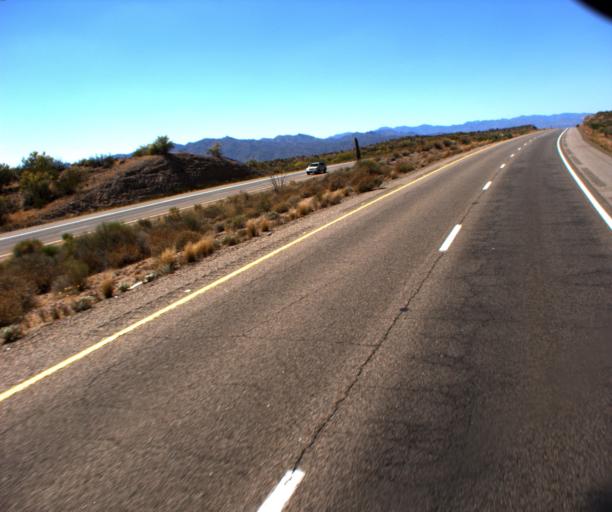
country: US
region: Arizona
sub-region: Yavapai County
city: Bagdad
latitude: 34.5870
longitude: -113.5073
